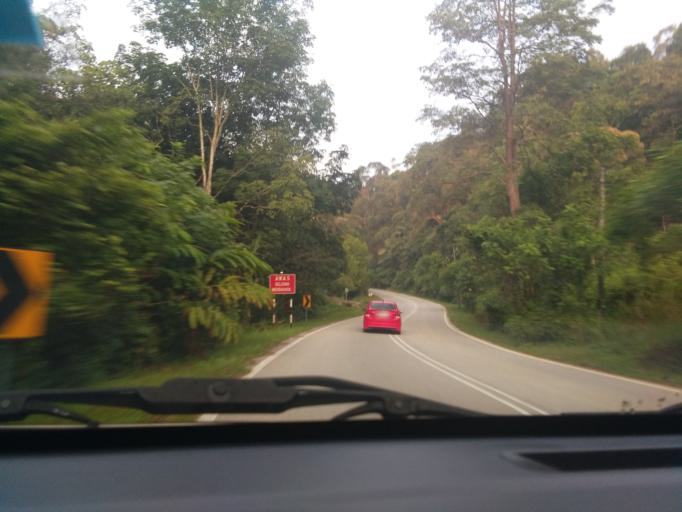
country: MY
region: Kedah
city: Kulim
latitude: 5.2906
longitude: 100.6498
